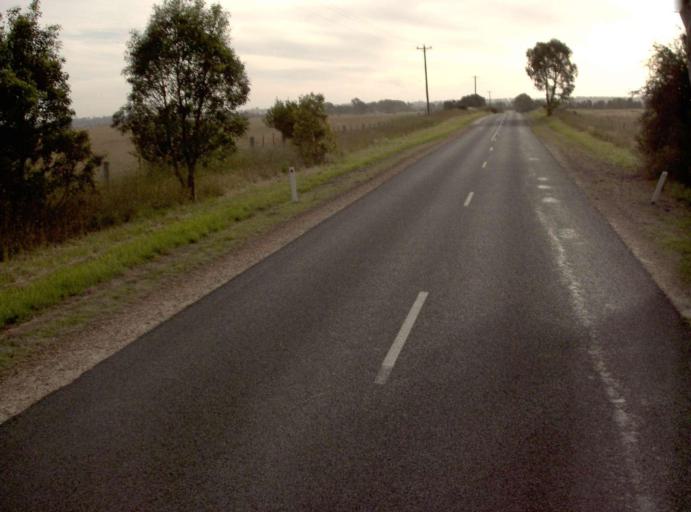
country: AU
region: Victoria
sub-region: Wellington
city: Sale
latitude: -37.8659
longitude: 147.0272
